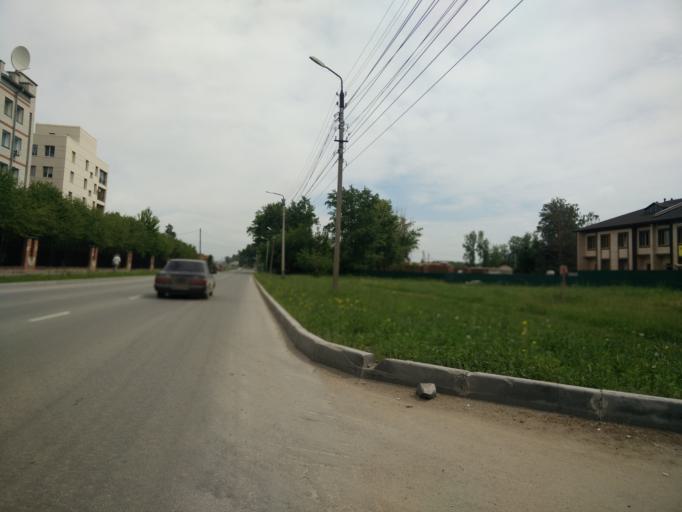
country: RU
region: Novosibirsk
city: Berdsk
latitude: 54.7703
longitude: 83.0725
